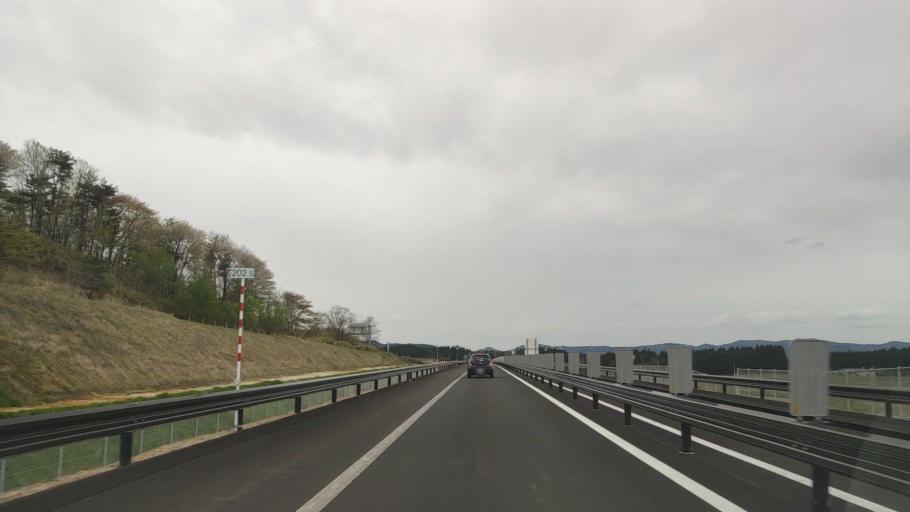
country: JP
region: Akita
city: Takanosu
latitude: 40.1997
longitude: 140.3621
